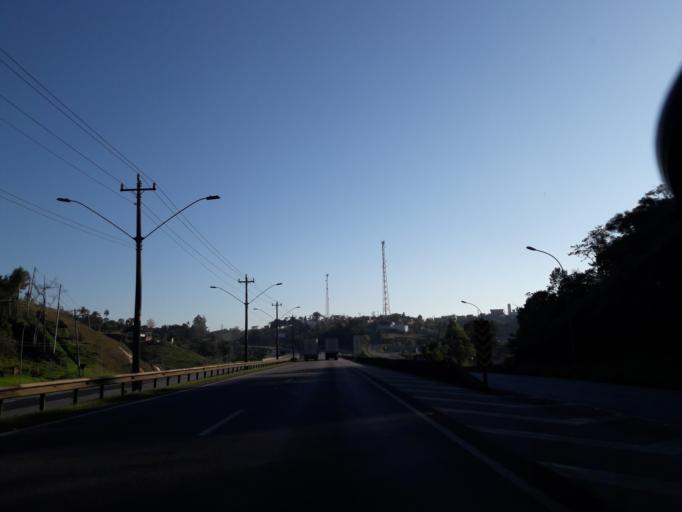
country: BR
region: Sao Paulo
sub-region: Sao Lourenco Da Serra
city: Sao Lourenco da Serra
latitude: -23.8571
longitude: -46.9423
